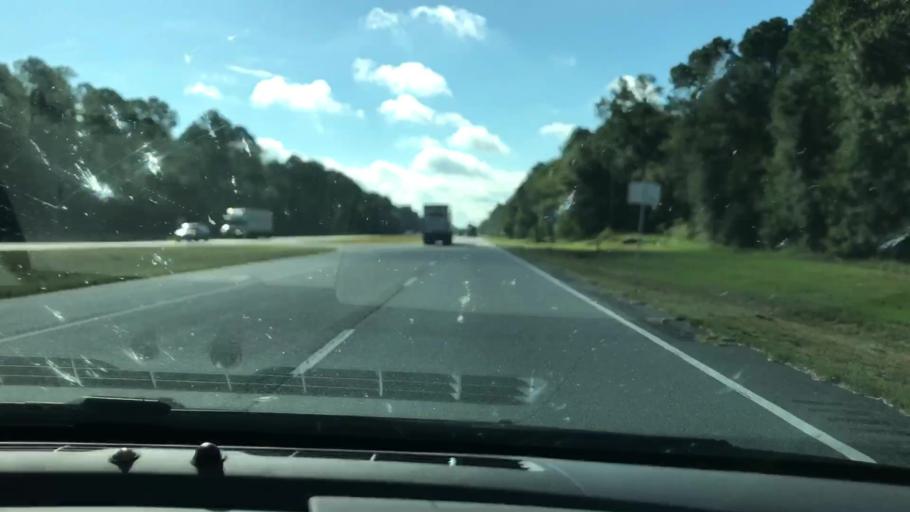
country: US
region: Georgia
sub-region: Dougherty County
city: Albany
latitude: 31.5668
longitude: -84.0189
